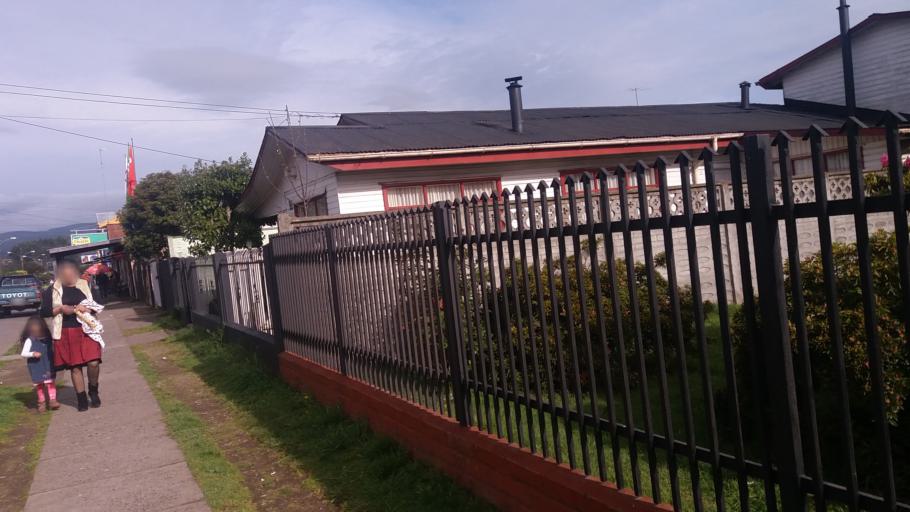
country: CL
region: Araucania
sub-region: Provincia de Cautin
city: Carahue
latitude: -39.1785
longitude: -73.1674
